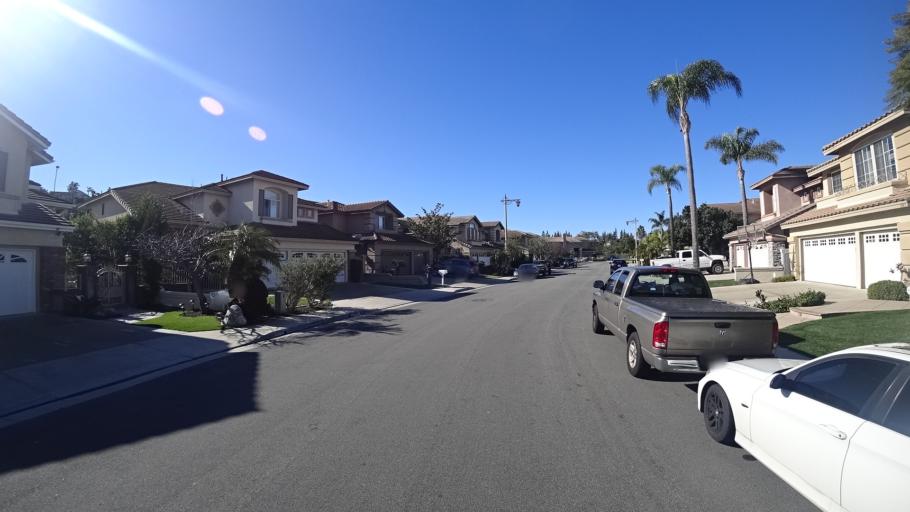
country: US
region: California
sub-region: Orange County
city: Villa Park
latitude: 33.8491
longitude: -117.7499
